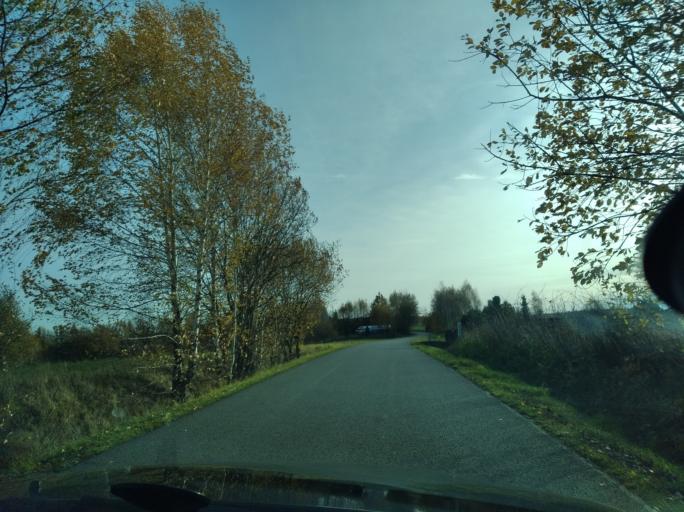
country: PL
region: Subcarpathian Voivodeship
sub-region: Powiat rzeszowski
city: Siedliska
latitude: 49.9345
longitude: 21.9752
